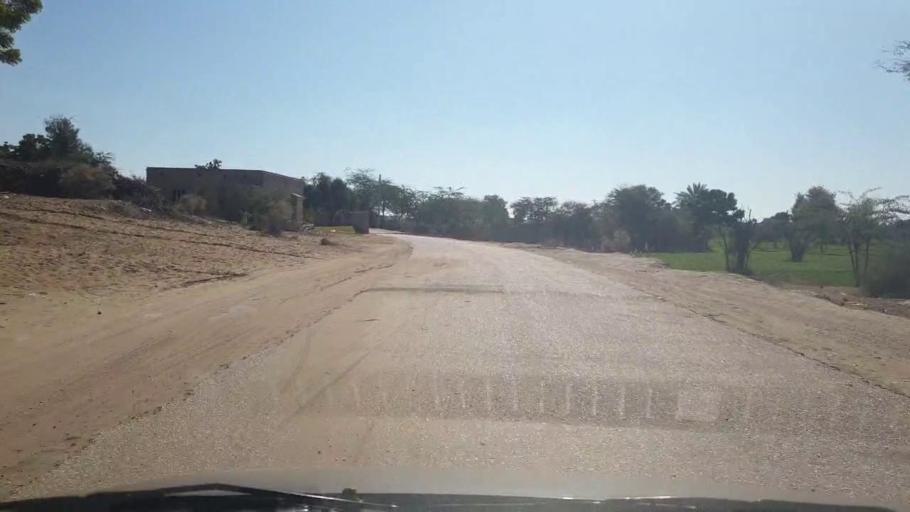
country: PK
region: Sindh
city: Bozdar
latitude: 27.0525
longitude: 68.6485
